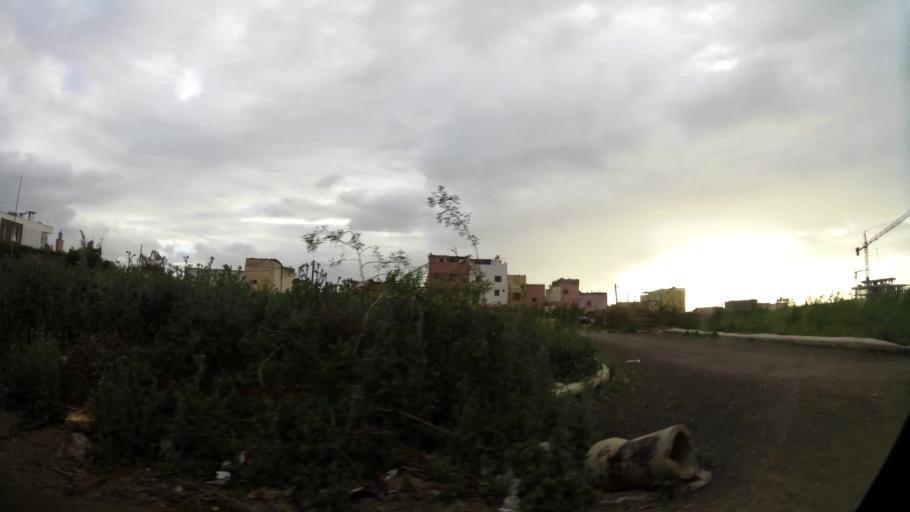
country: MA
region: Grand Casablanca
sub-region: Casablanca
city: Casablanca
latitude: 33.5780
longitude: -7.6806
